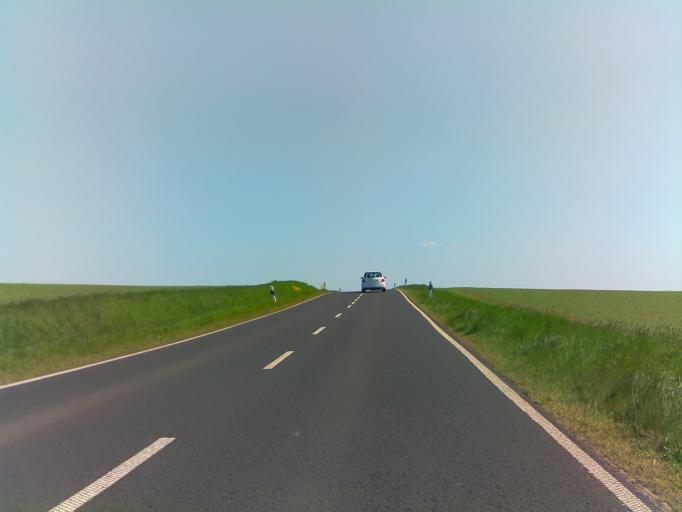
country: DE
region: Hesse
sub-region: Regierungsbezirk Darmstadt
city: Birstein
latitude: 50.3708
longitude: 9.3030
